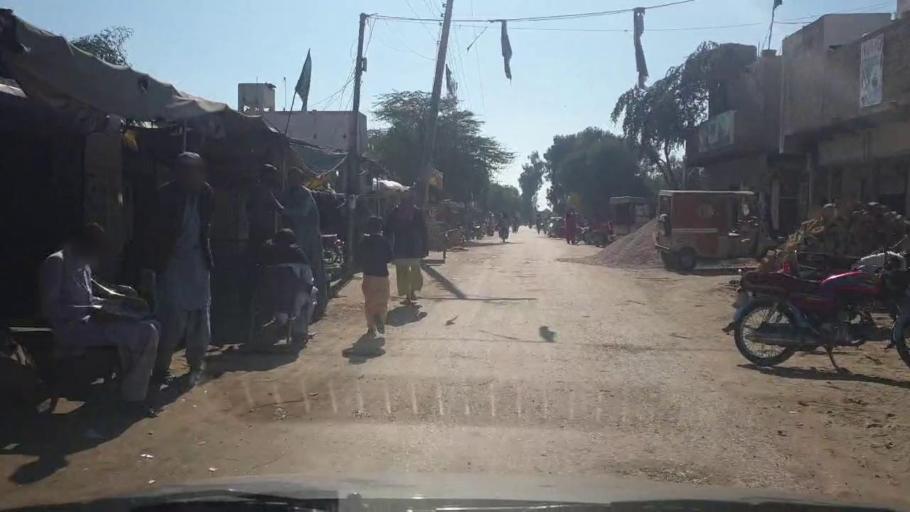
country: PK
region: Sindh
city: Bozdar
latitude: 27.1829
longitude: 68.6389
